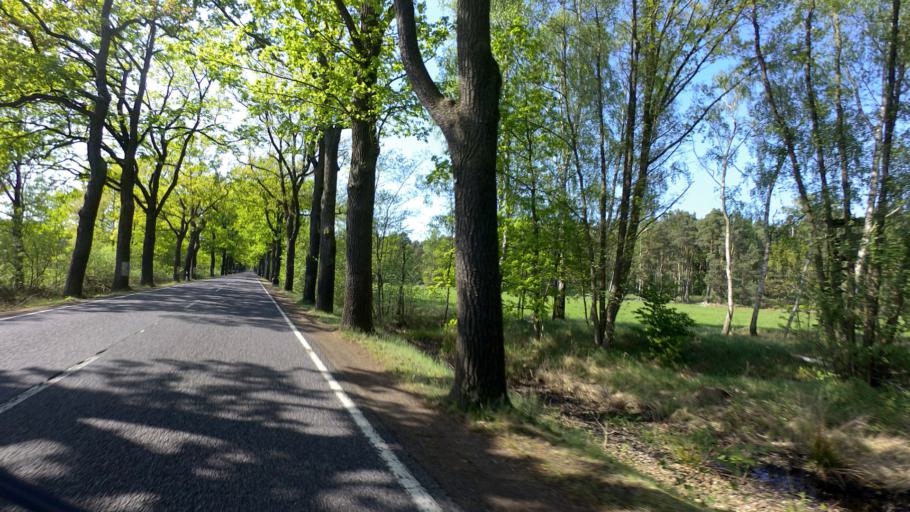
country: DE
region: Brandenburg
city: Munchehofe
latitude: 52.0957
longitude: 13.8414
